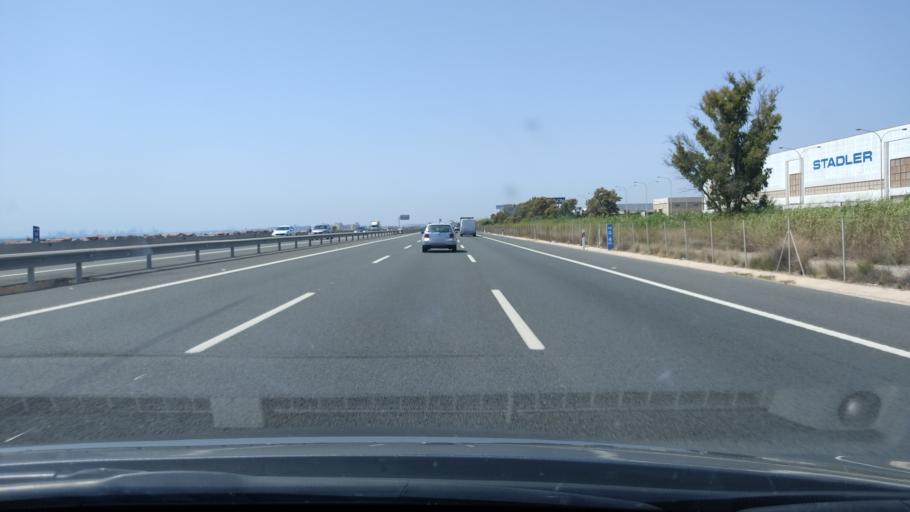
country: ES
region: Valencia
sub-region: Provincia de Valencia
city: Albuixech
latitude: 39.5434
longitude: -0.3017
